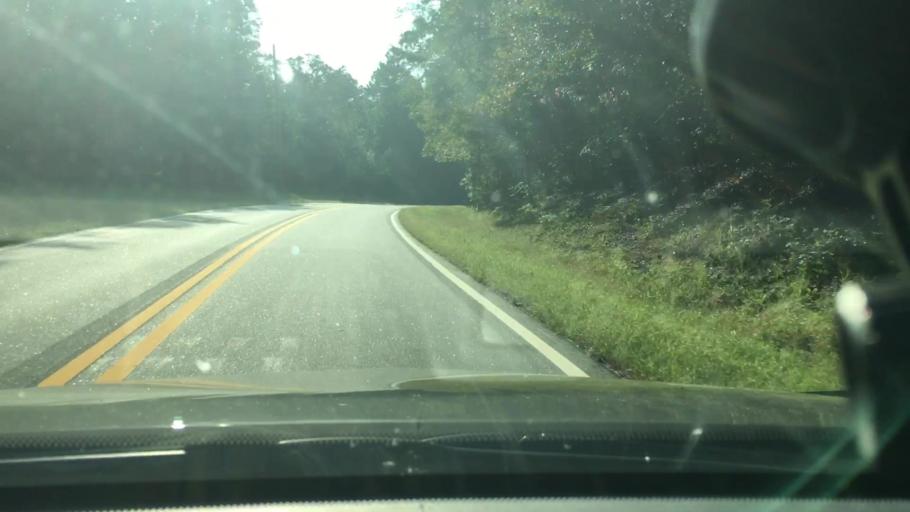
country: US
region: North Carolina
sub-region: Rutherford County
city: Rutherfordton
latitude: 35.3296
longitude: -82.0595
